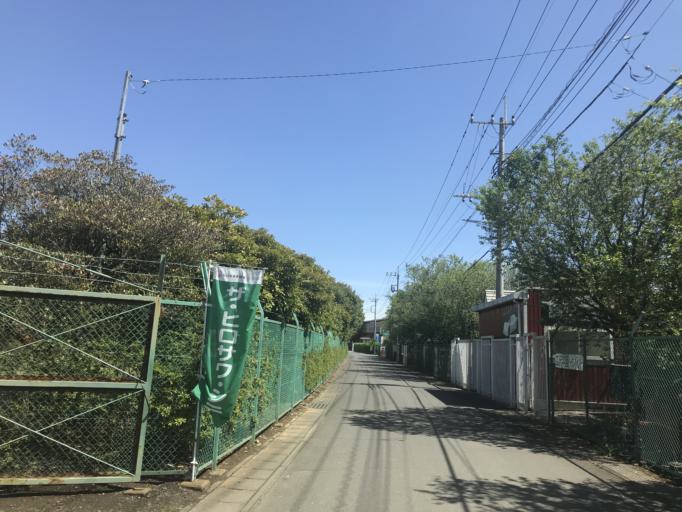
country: JP
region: Ibaraki
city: Shimodate
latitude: 36.2939
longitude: 140.0193
